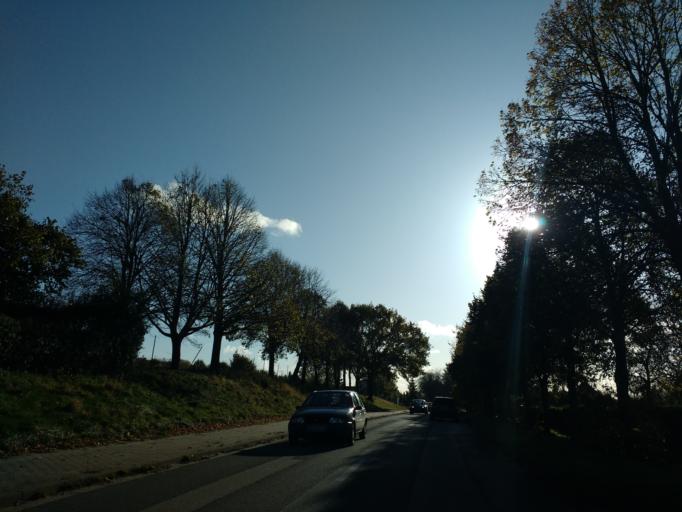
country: DE
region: Mecklenburg-Vorpommern
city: Klutz
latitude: 53.9547
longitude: 11.1640
